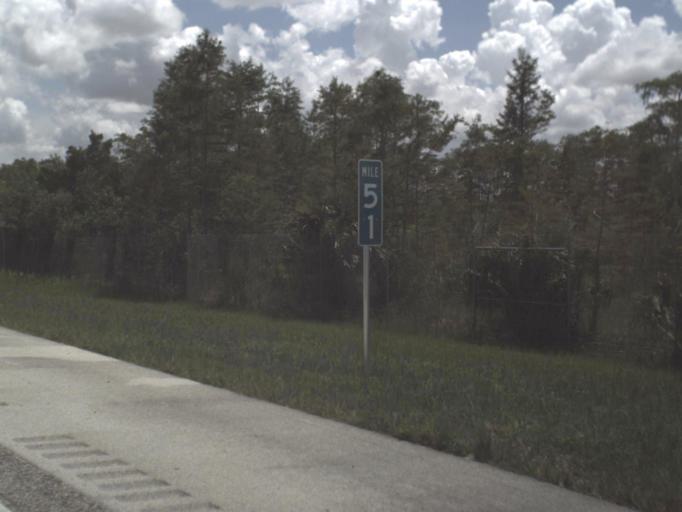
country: US
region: Florida
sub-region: Broward County
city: Weston
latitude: 26.1725
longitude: -80.8829
